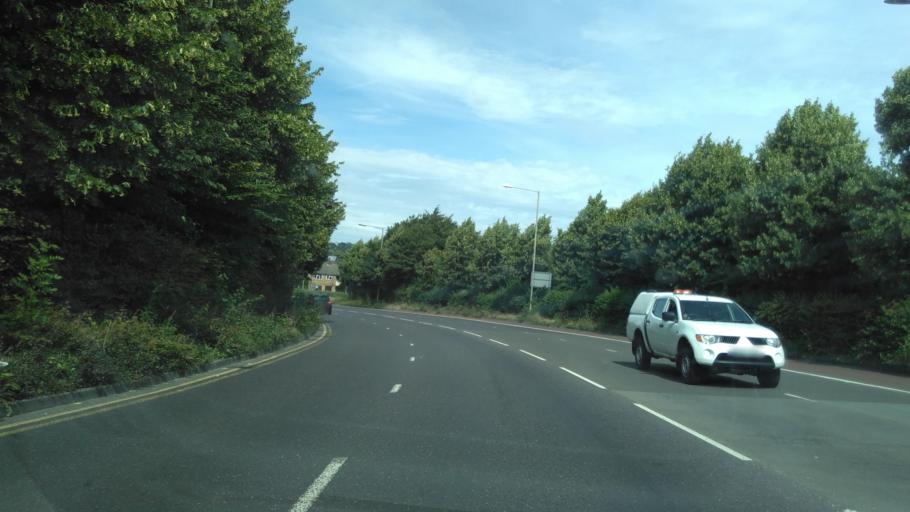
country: GB
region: England
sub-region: Kent
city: Canterbury
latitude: 51.2837
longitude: 1.0896
